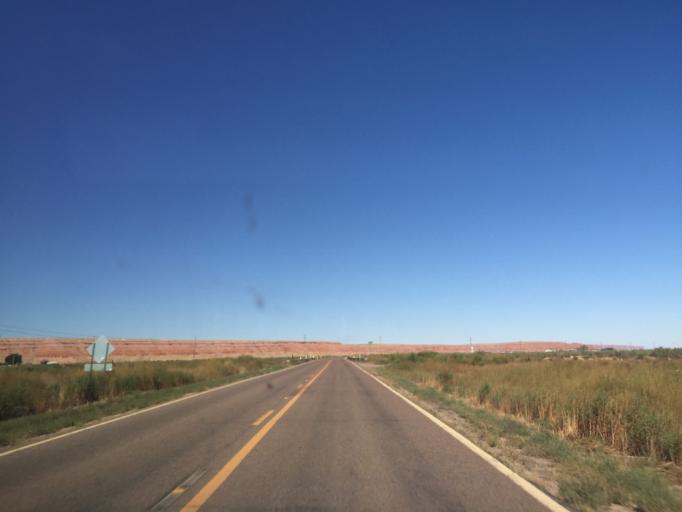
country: US
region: Arizona
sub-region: Apache County
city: Many Farms
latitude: 36.3319
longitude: -109.6227
